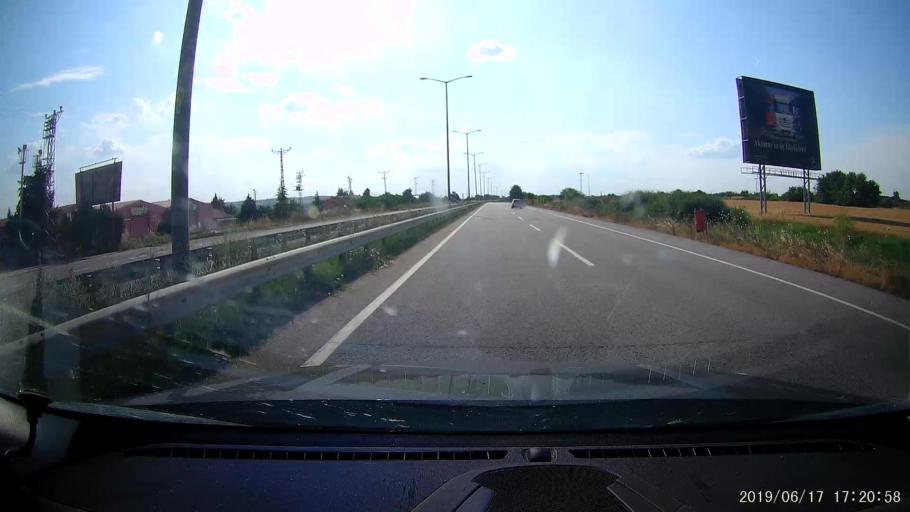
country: GR
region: East Macedonia and Thrace
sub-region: Nomos Evrou
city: Rizia
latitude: 41.7042
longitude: 26.4027
